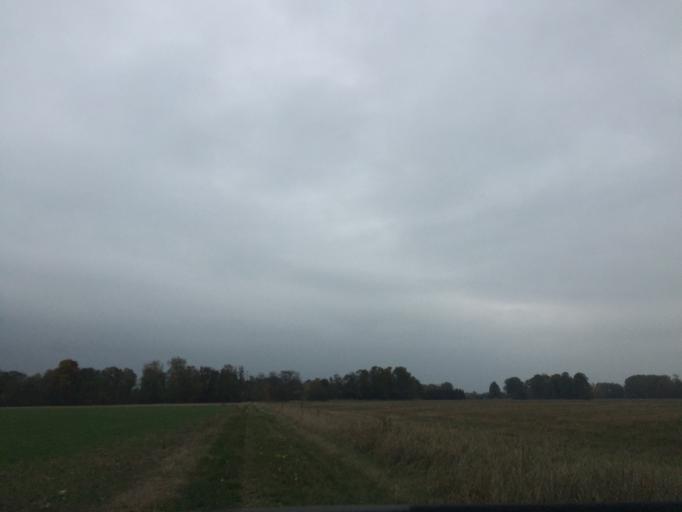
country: LV
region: Dobeles Rajons
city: Dobele
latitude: 56.6750
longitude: 23.4366
